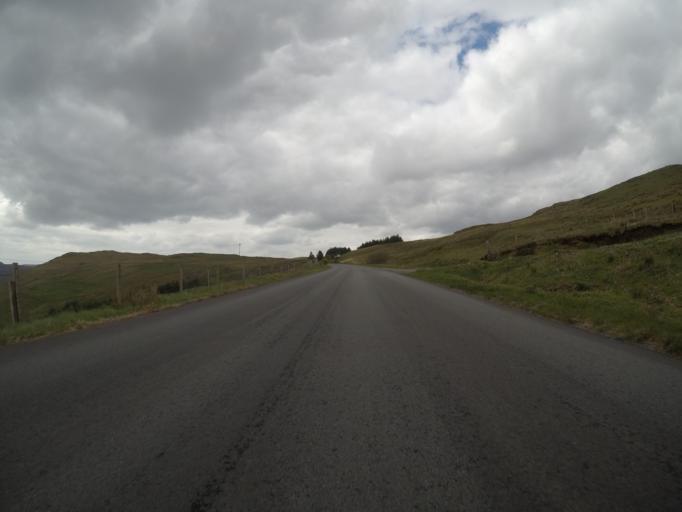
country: GB
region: Scotland
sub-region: Highland
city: Isle of Skye
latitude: 57.3300
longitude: -6.3382
